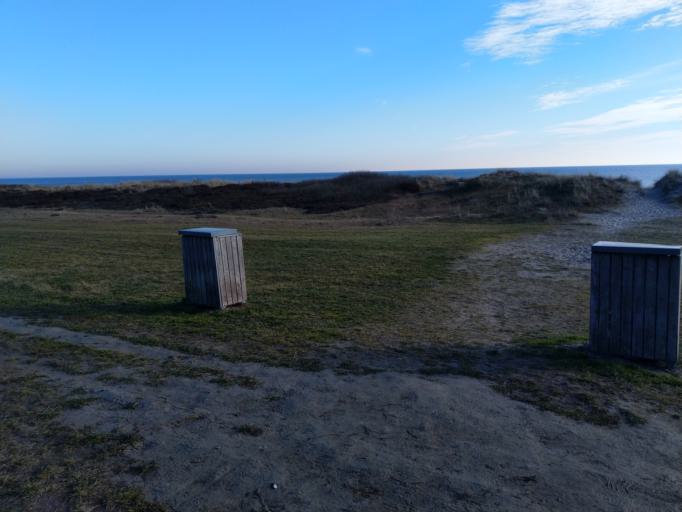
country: DK
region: Zealand
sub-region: Guldborgsund Kommune
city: Nykobing Falster
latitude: 54.6537
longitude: 11.9596
